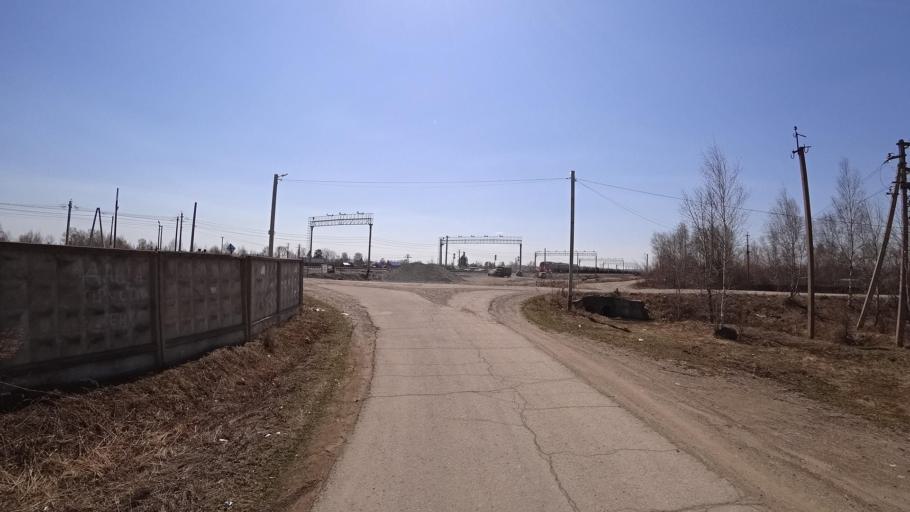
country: RU
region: Khabarovsk Krai
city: Khurba
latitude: 50.4124
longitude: 136.8808
